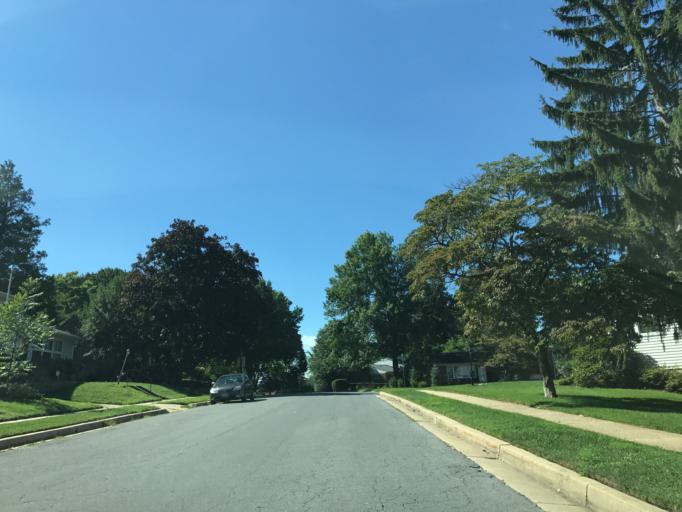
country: US
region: Maryland
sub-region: Howard County
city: Ilchester
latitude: 39.2660
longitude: -76.7588
